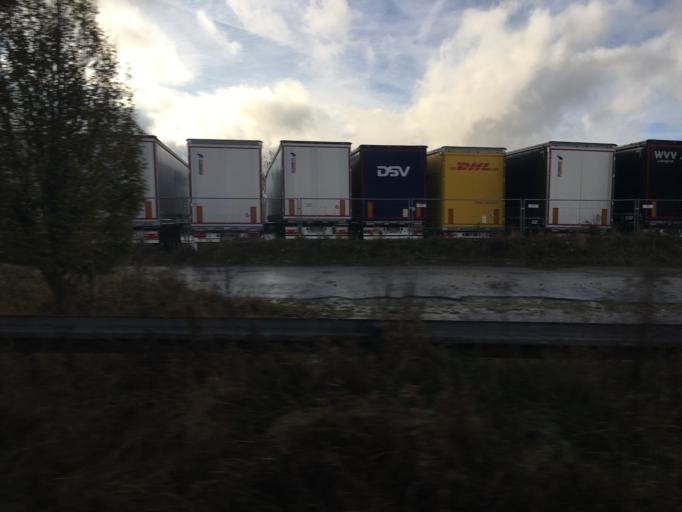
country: DE
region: North Rhine-Westphalia
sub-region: Regierungsbezirk Munster
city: Nordwalde
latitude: 52.0762
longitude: 7.4625
